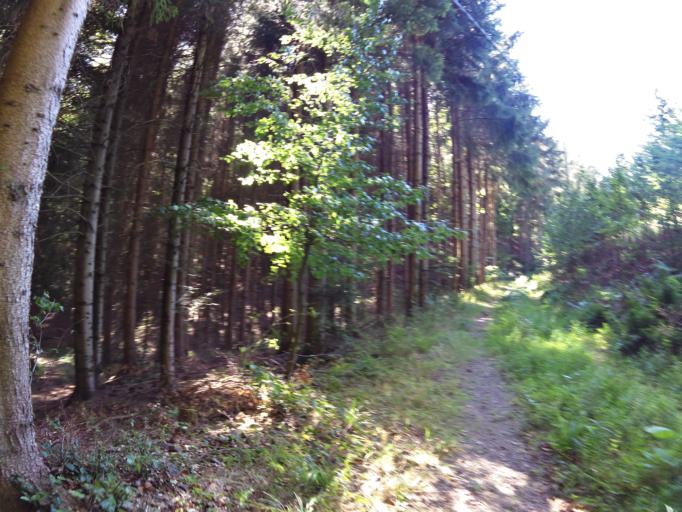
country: DE
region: Baden-Wuerttemberg
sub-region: Freiburg Region
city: Hohberg
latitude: 48.3229
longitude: 7.9035
